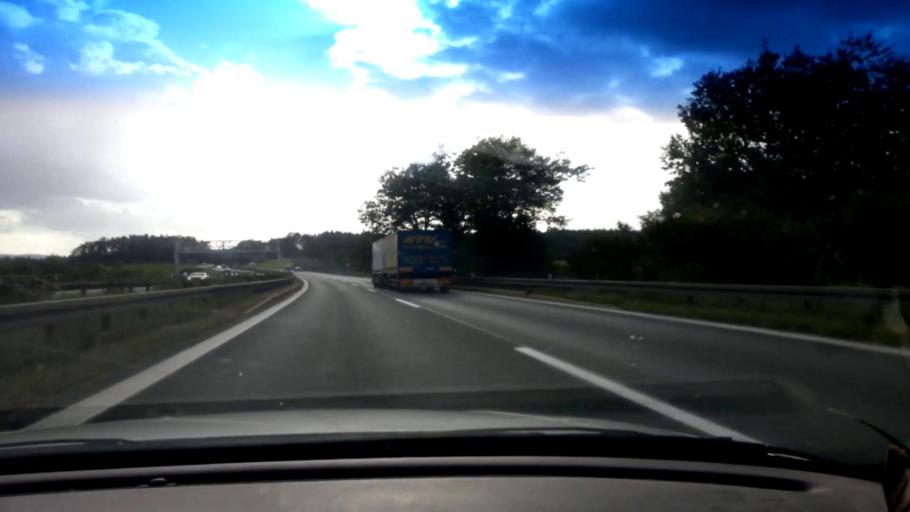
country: DE
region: Bavaria
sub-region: Upper Franconia
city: Eckersdorf
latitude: 50.0267
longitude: 11.4401
